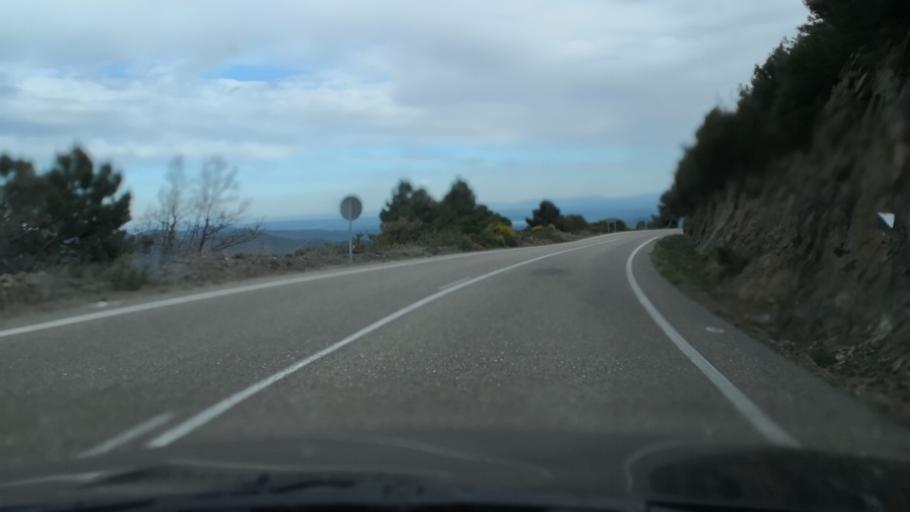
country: ES
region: Extremadura
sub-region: Provincia de Caceres
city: Acebo
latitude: 40.2444
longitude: -6.6852
